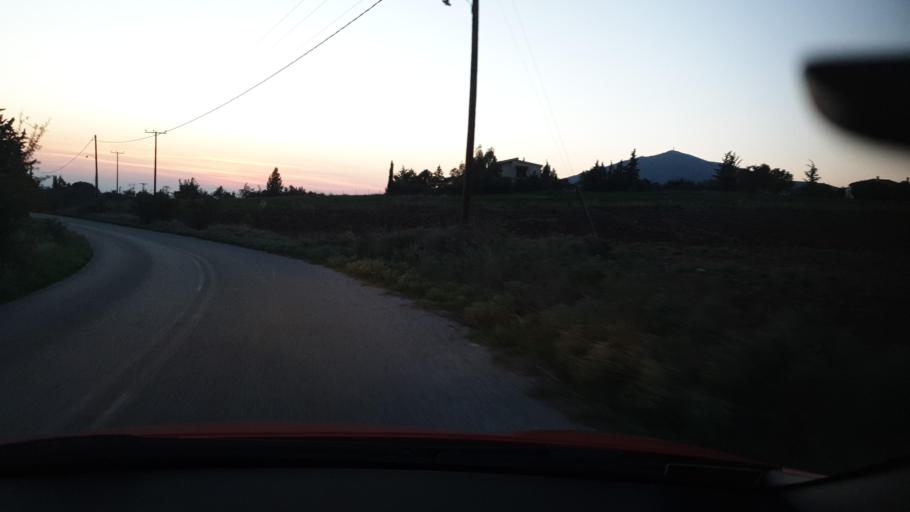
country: GR
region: Central Macedonia
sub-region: Nomos Thessalonikis
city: Vasilika
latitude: 40.5092
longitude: 23.1396
